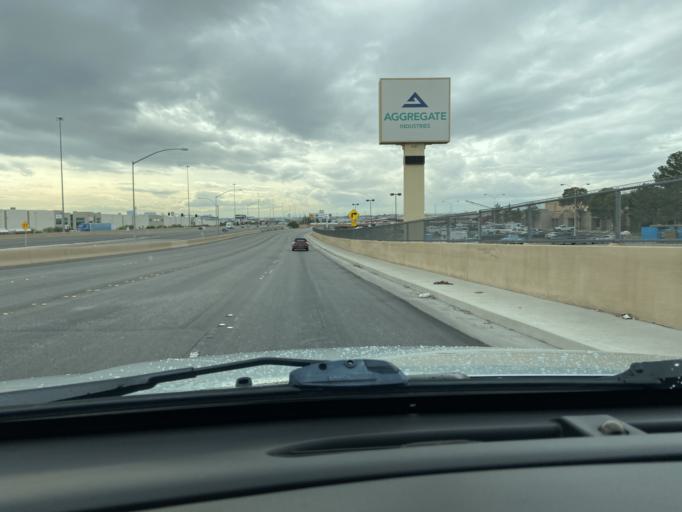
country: US
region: Nevada
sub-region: Clark County
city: North Las Vegas
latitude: 36.2389
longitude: -115.1047
